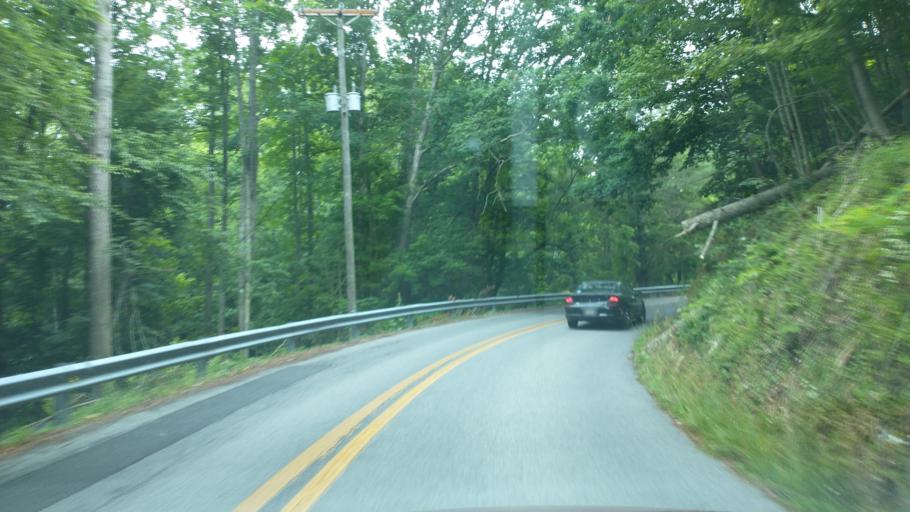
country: US
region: West Virginia
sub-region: Mercer County
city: Athens
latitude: 37.4228
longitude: -81.0046
